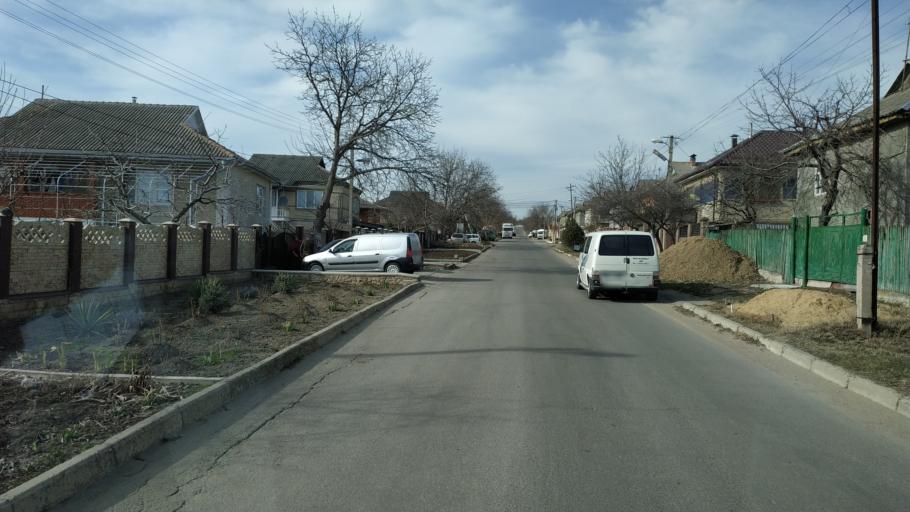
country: MD
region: Chisinau
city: Vatra
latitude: 47.0762
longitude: 28.6912
